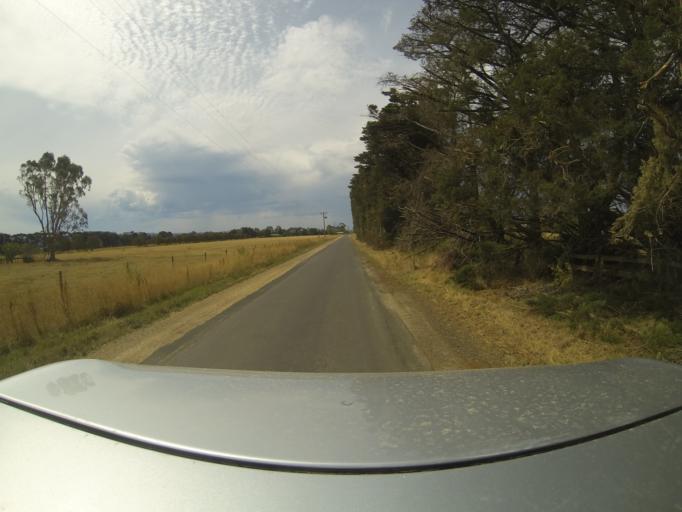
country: AU
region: Victoria
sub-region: Wellington
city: Heyfield
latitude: -38.0128
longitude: 146.6871
